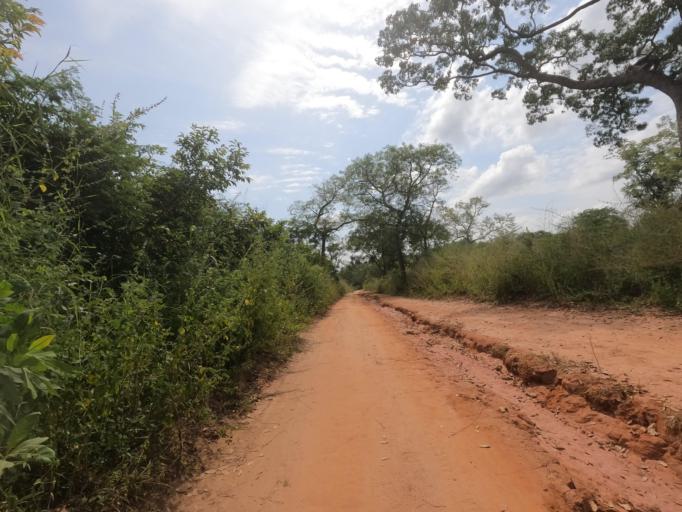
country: GW
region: Oio
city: Bissora
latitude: 12.3679
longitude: -15.7053
